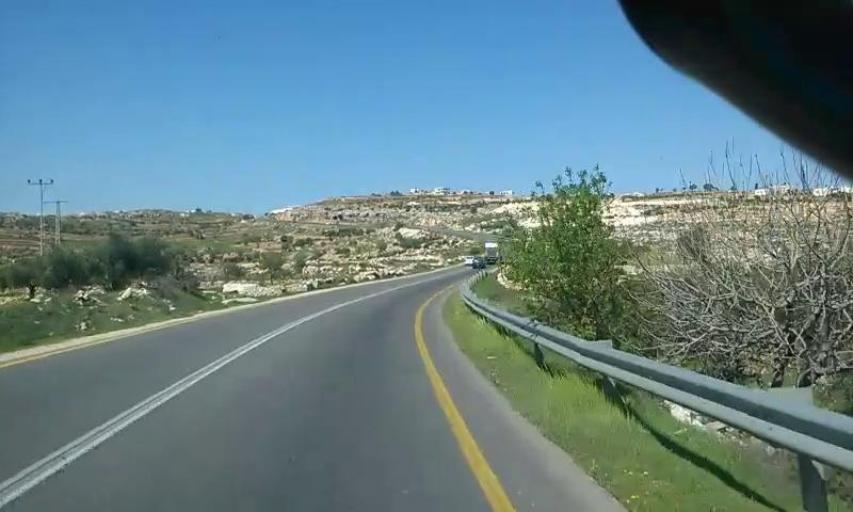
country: PS
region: West Bank
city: Marah Rabbah
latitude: 31.6472
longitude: 35.1834
